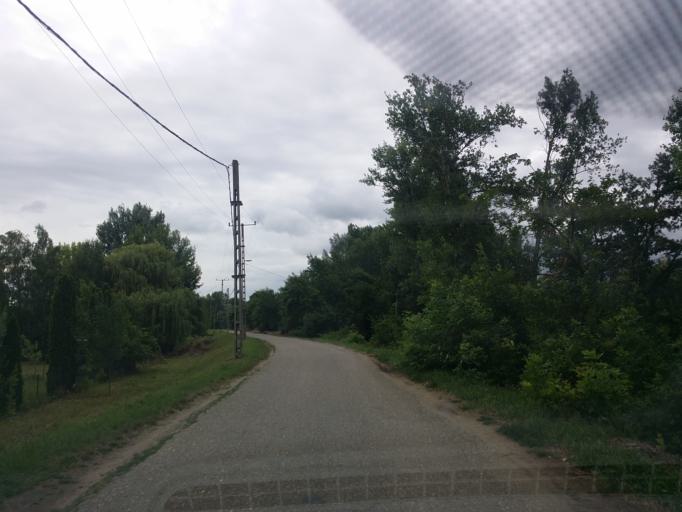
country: HU
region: Heves
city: Tiszanana
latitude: 47.5824
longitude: 20.6072
